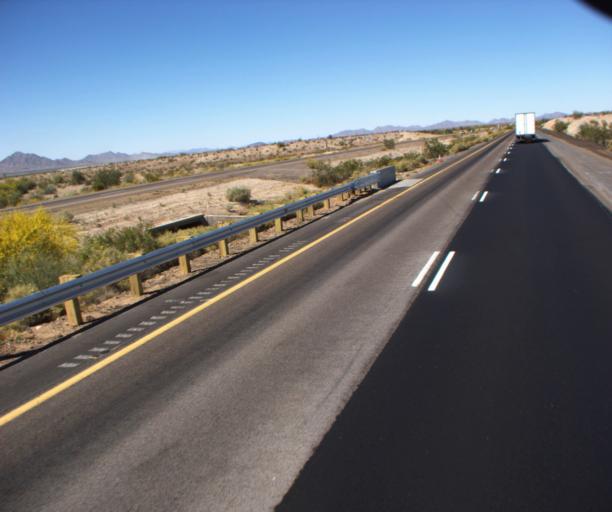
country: US
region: Arizona
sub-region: Maricopa County
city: Gila Bend
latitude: 33.0598
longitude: -112.6445
